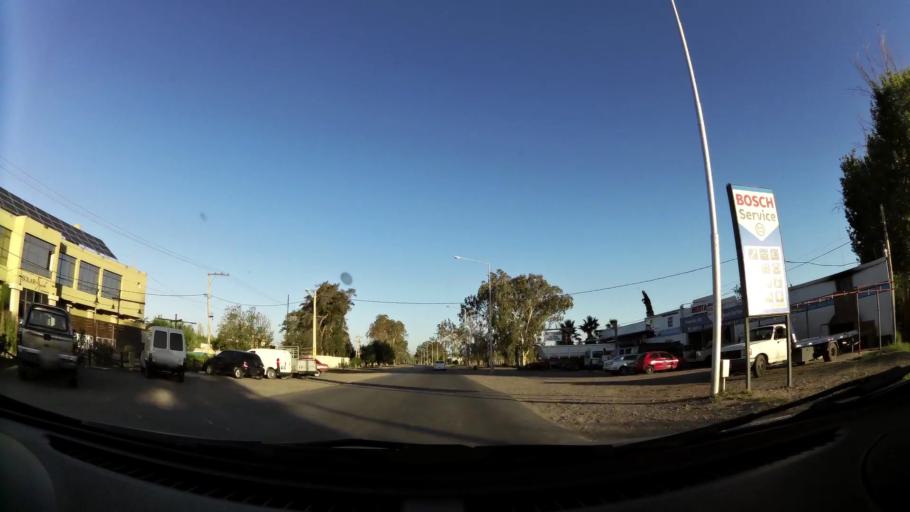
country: AR
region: San Juan
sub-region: Departamento de Santa Lucia
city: Santa Lucia
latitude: -31.5451
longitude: -68.4903
